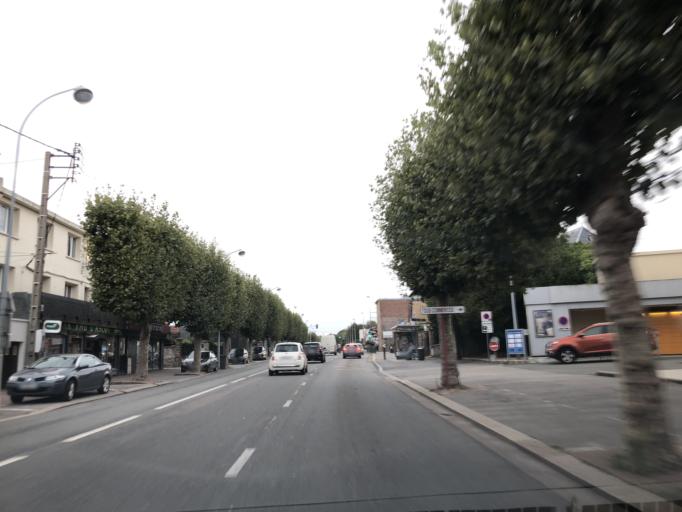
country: FR
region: Haute-Normandie
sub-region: Departement de la Seine-Maritime
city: Rouxmesnil-Bouteilles
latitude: 49.9161
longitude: 1.0745
